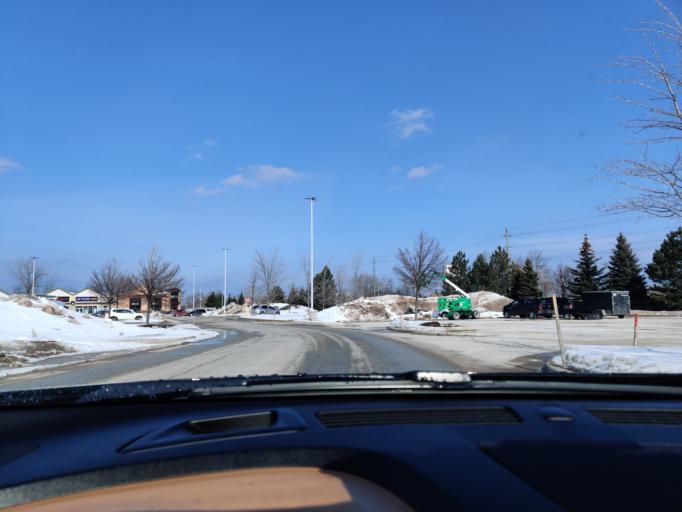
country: CA
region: Ontario
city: Collingwood
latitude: 44.5040
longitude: -80.2361
